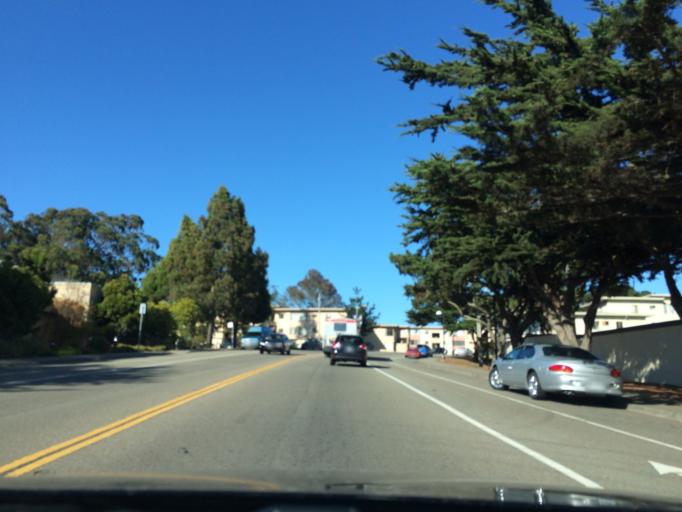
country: US
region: California
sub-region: San Mateo County
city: Daly City
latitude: 37.7280
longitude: -122.4807
